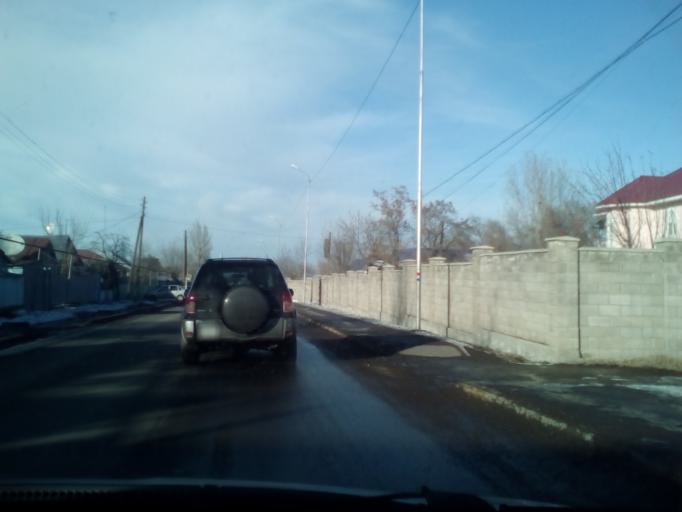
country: KZ
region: Almaty Oblysy
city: Burunday
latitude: 43.1737
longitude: 76.4155
